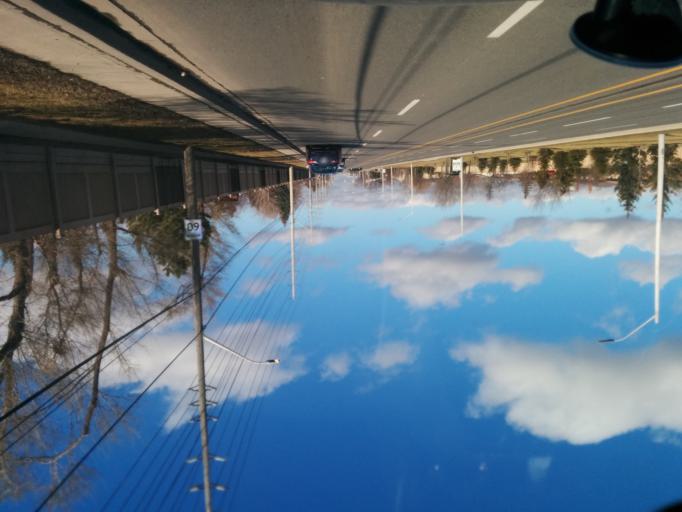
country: CA
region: Ontario
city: Mississauga
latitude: 43.6030
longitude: -79.6240
